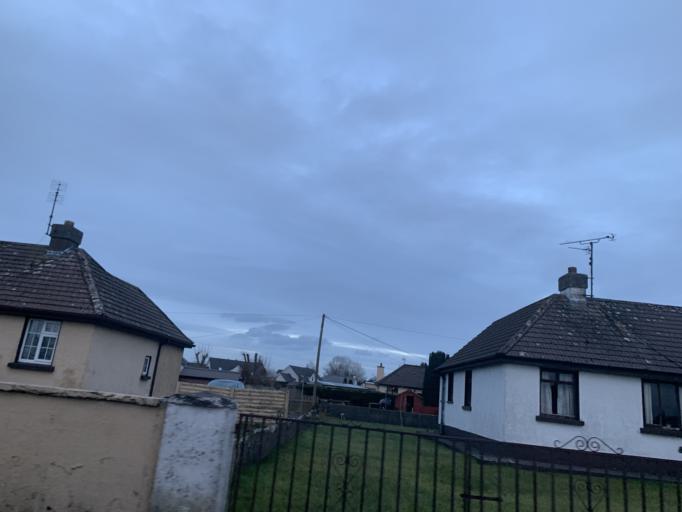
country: IE
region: Connaught
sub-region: Sligo
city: Collooney
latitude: 54.1820
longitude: -8.4919
